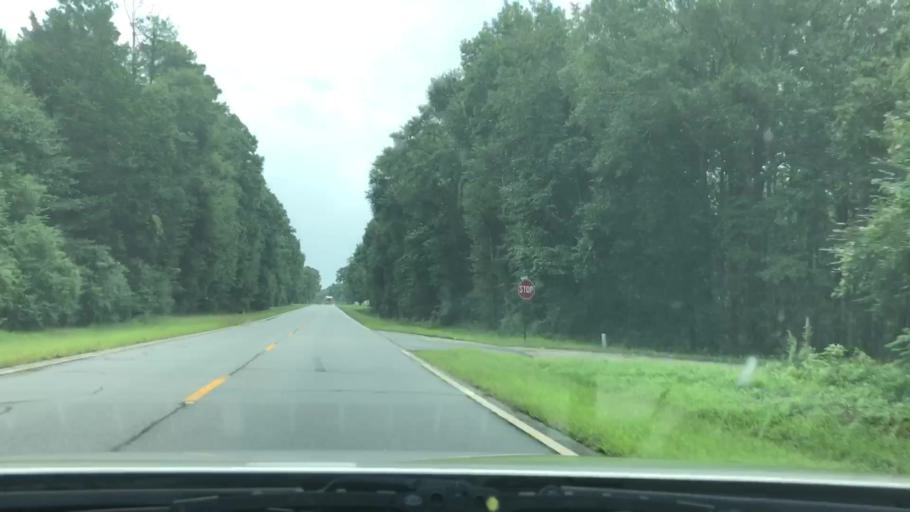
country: US
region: Georgia
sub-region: Pike County
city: Zebulon
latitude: 33.0895
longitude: -84.2749
